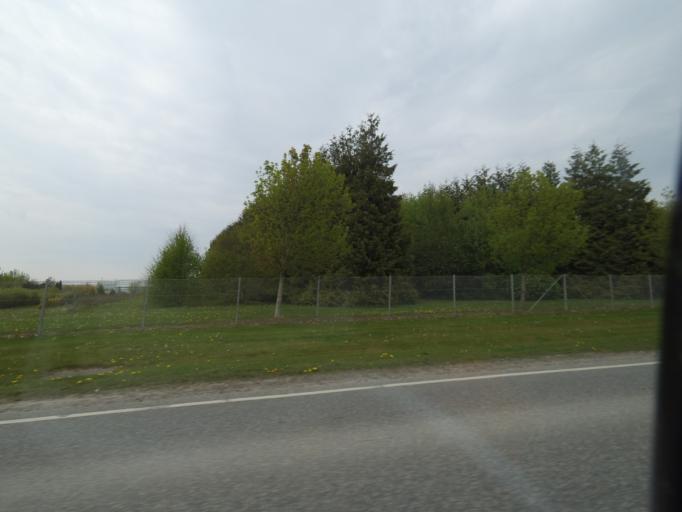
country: DK
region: South Denmark
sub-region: Faaborg-Midtfyn Kommune
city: Arslev
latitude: 55.3047
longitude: 10.4426
